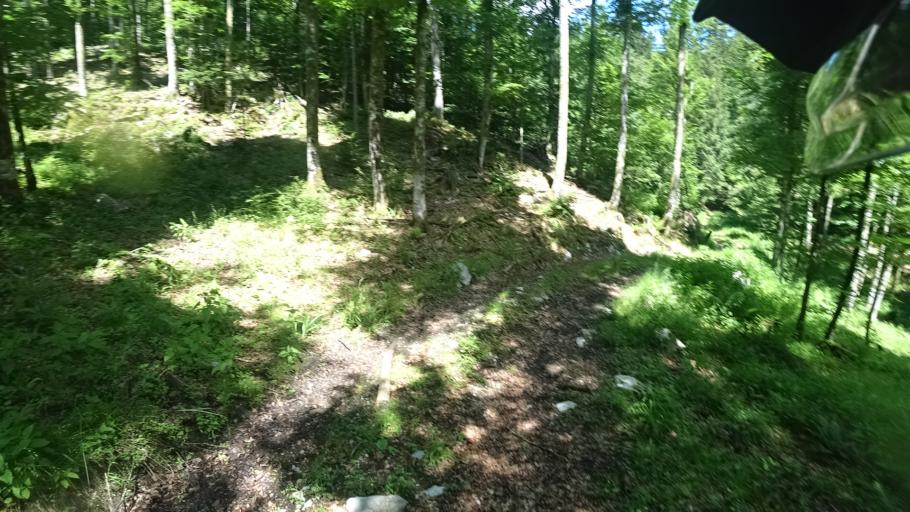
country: SI
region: Osilnica
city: Osilnica
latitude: 45.4833
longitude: 14.7185
